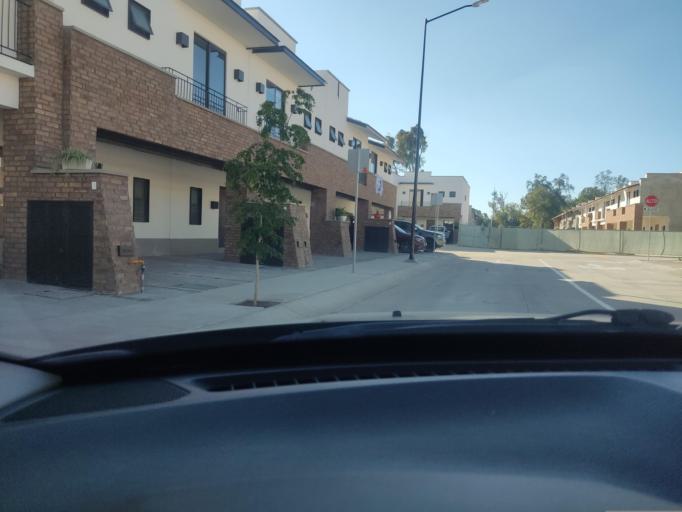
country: MX
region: Guanajuato
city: Leon
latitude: 21.1544
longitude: -101.6627
